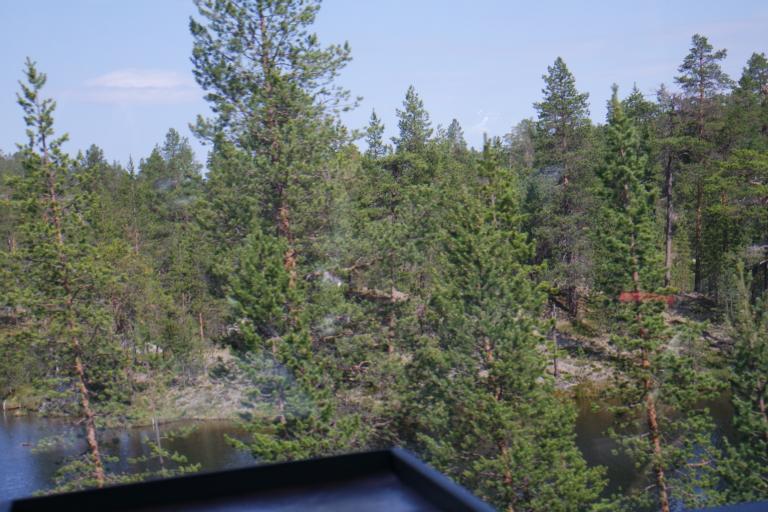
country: FI
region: Lapland
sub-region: Pohjois-Lappi
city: Ivalo
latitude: 68.8155
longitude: 27.3402
